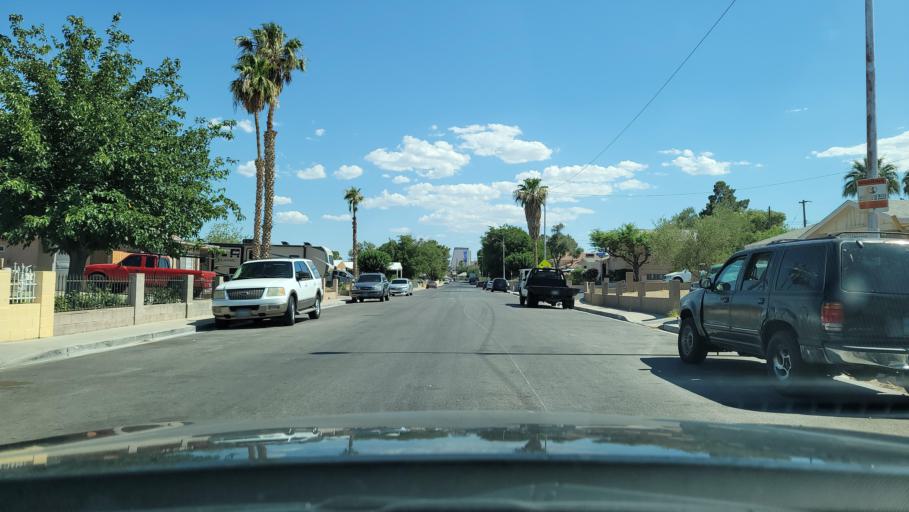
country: US
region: Nevada
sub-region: Clark County
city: Las Vegas
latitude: 36.1991
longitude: -115.1450
